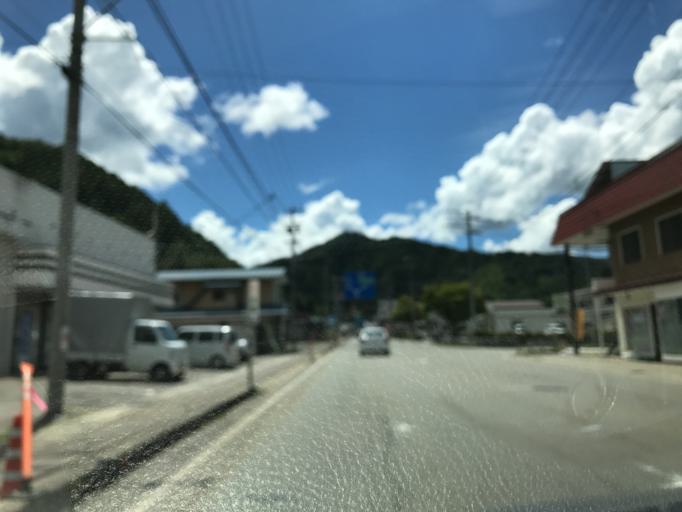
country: JP
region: Gifu
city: Takayama
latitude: 36.1310
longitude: 137.1912
